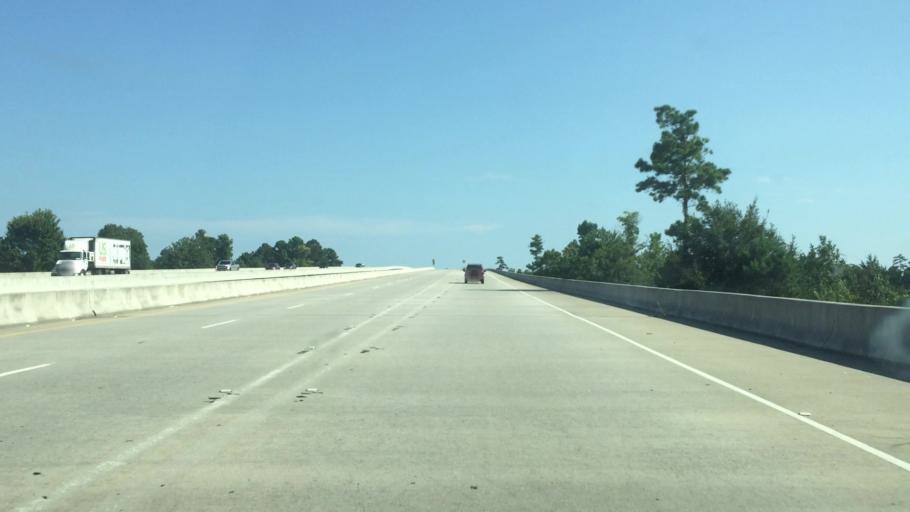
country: US
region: South Carolina
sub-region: Horry County
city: North Myrtle Beach
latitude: 33.7940
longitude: -78.7787
